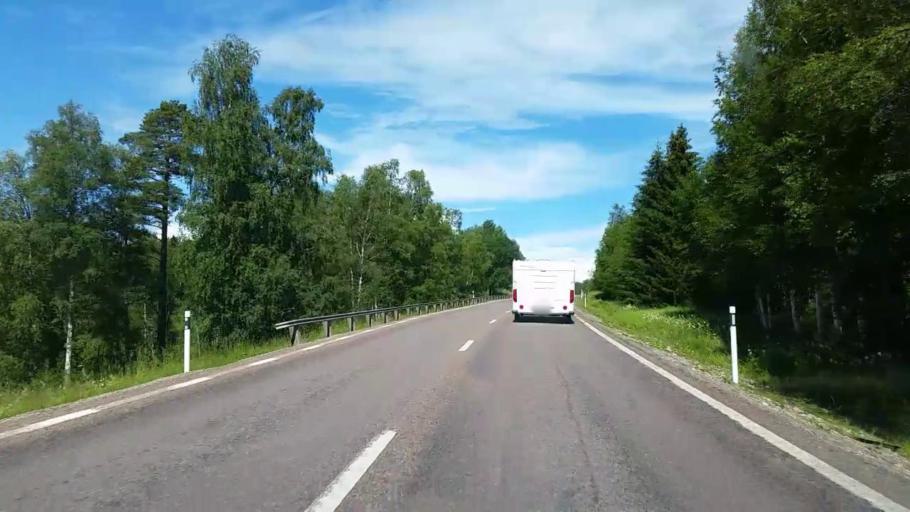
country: SE
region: Dalarna
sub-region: Rattviks Kommun
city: Raettvik
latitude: 60.9946
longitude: 15.2173
